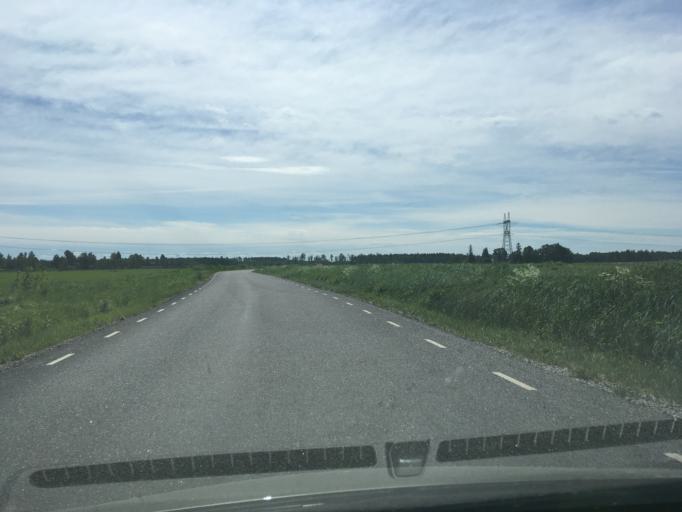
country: EE
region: Paernumaa
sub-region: Audru vald
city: Audru
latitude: 58.4369
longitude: 24.3980
